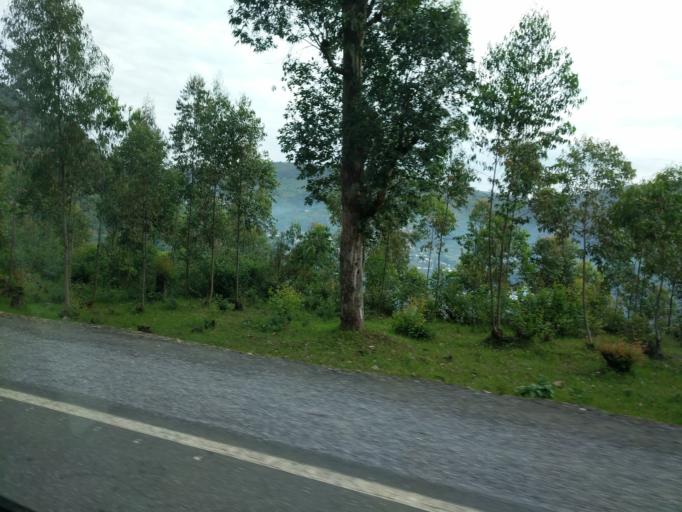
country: RW
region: Kigali
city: Kigali
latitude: -1.7782
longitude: 29.9277
